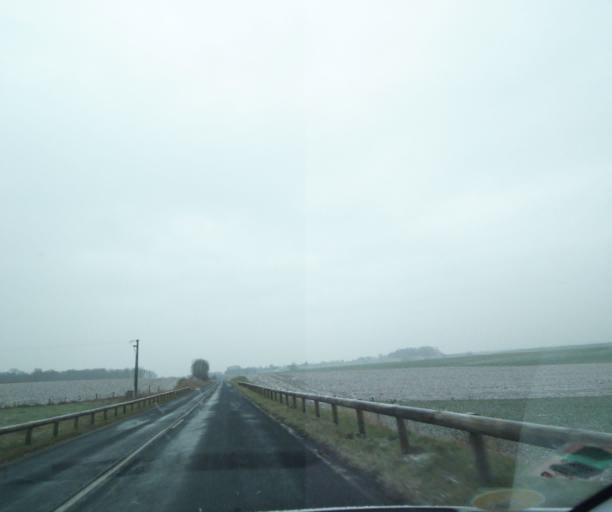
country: FR
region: Champagne-Ardenne
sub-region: Departement de la Haute-Marne
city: Wassy
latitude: 48.4700
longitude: 5.0239
